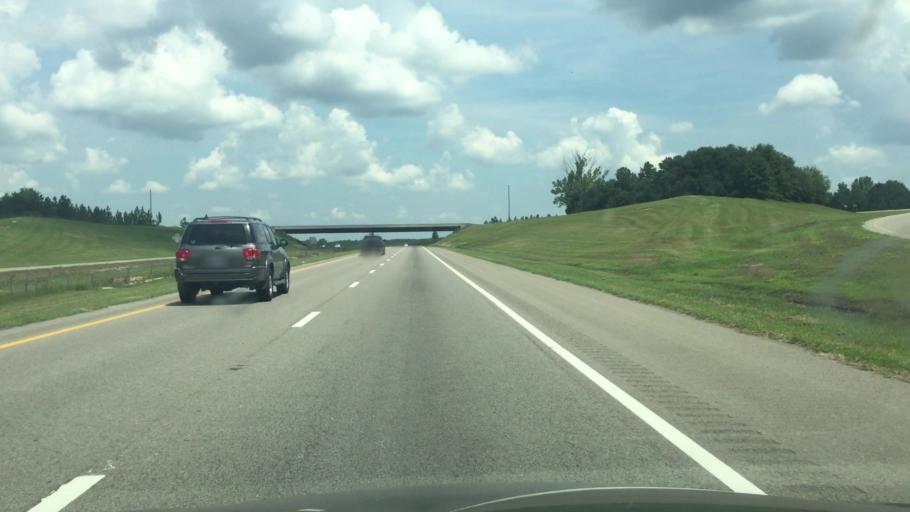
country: US
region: North Carolina
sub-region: Richmond County
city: Ellerbe
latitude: 35.1705
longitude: -79.7145
